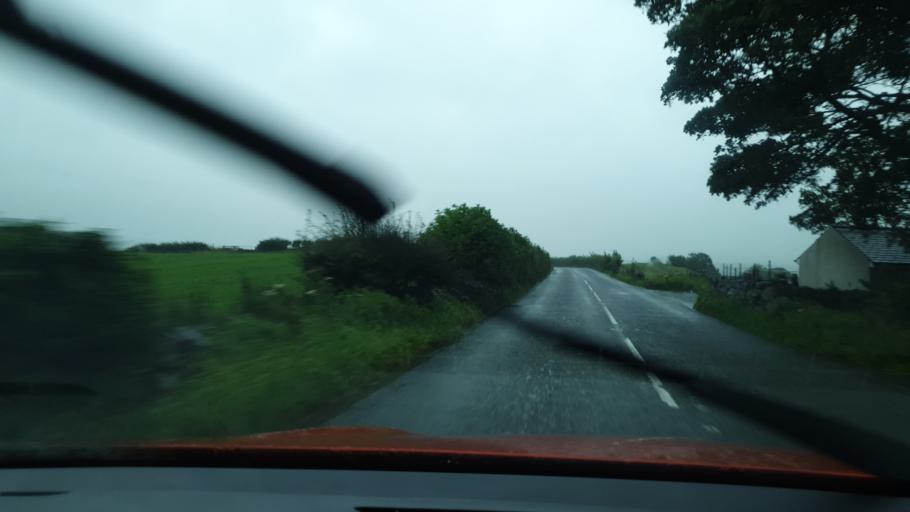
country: GB
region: England
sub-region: Cumbria
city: Millom
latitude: 54.2760
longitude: -3.2209
